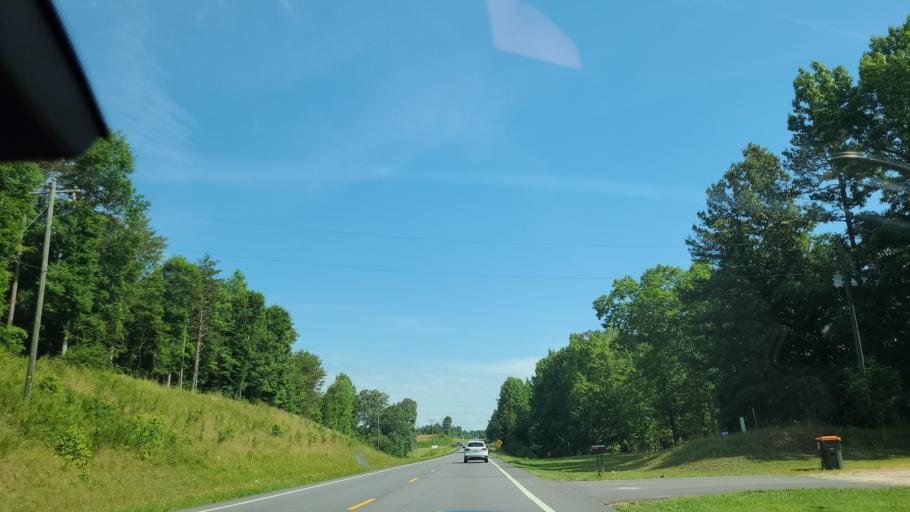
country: US
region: South Carolina
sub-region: Oconee County
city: Walhalla
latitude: 34.7173
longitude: -83.0536
